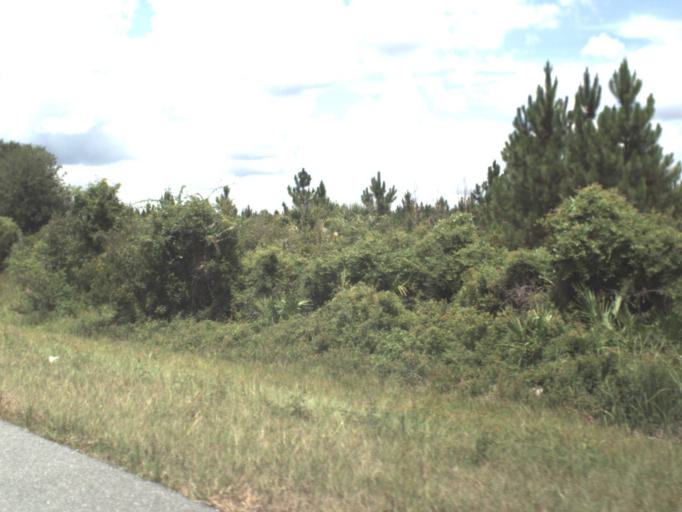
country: US
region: Florida
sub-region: Taylor County
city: Perry
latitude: 30.1429
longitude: -83.8444
